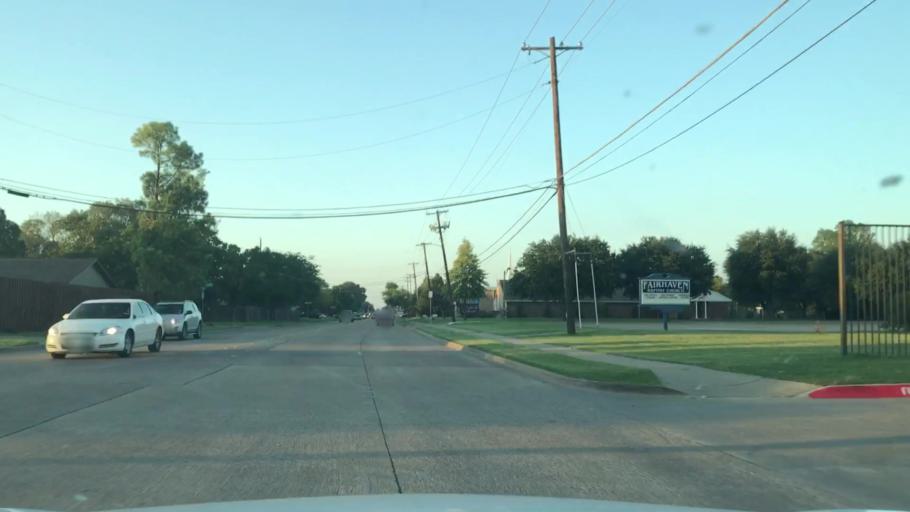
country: US
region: Texas
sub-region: Dallas County
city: Mesquite
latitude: 32.7465
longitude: -96.5834
